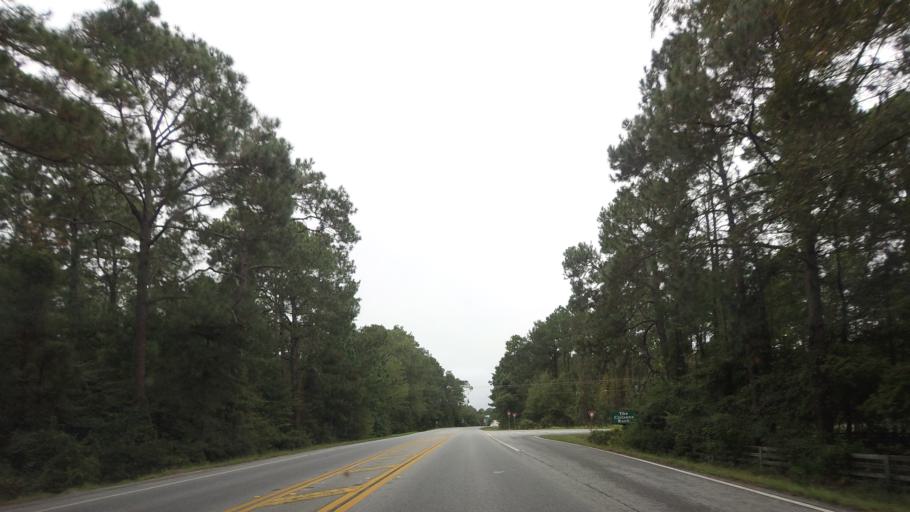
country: US
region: Georgia
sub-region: Berrien County
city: Nashville
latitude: 31.1902
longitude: -83.2483
